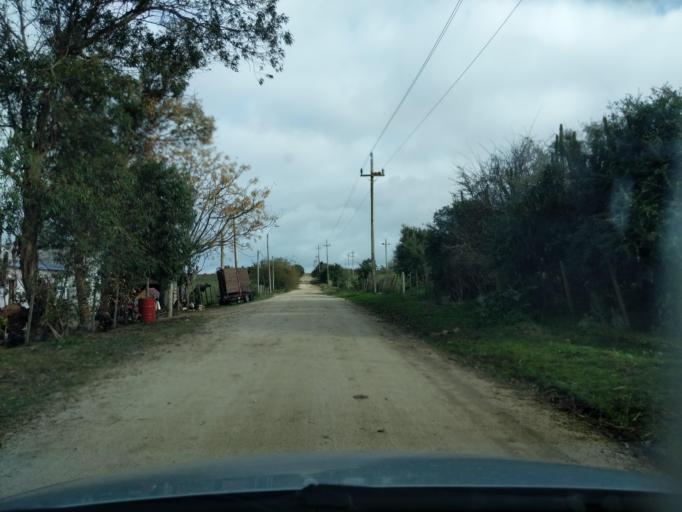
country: UY
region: Florida
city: Florida
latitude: -34.0580
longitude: -56.2201
